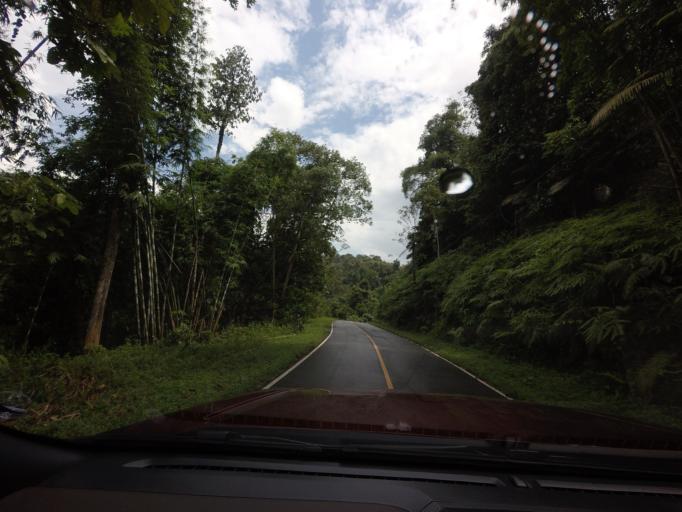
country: TH
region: Narathiwat
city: Sukhirin
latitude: 5.9269
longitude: 101.6480
